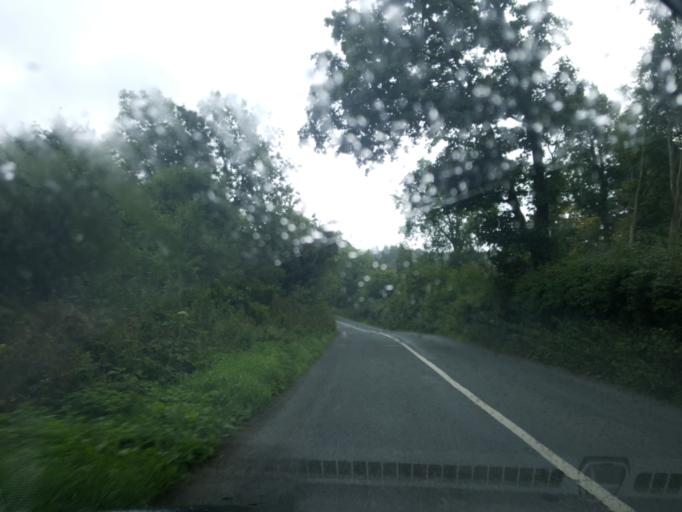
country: IE
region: Leinster
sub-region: Wicklow
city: Valleymount
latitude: 53.1284
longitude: -6.5869
